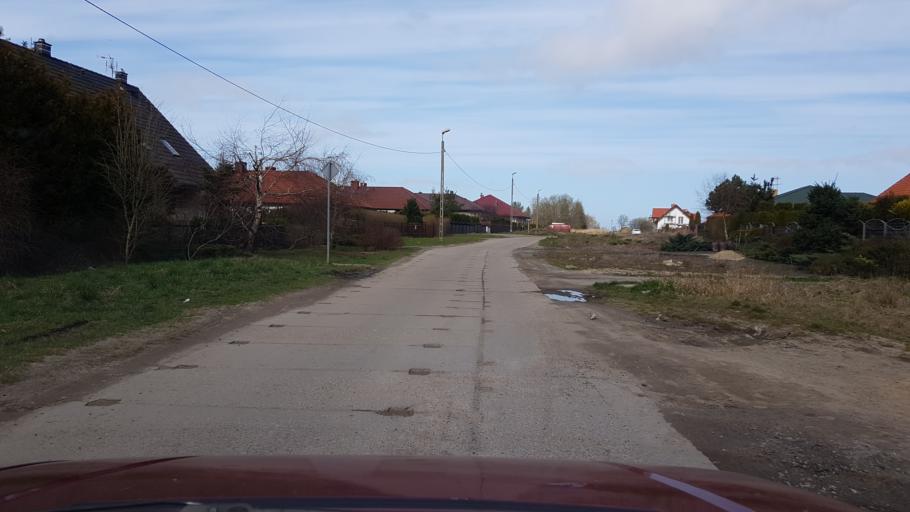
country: PL
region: West Pomeranian Voivodeship
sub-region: Koszalin
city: Koszalin
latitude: 54.2197
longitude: 16.1691
